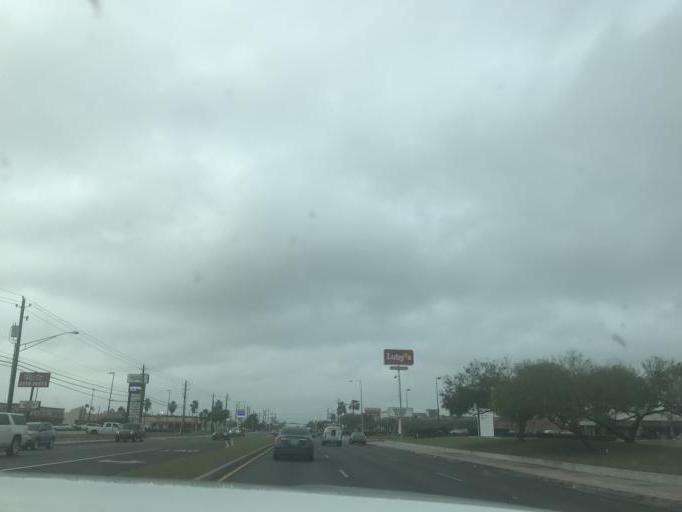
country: US
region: Texas
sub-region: Nueces County
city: Corpus Christi
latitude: 27.6834
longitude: -97.3795
